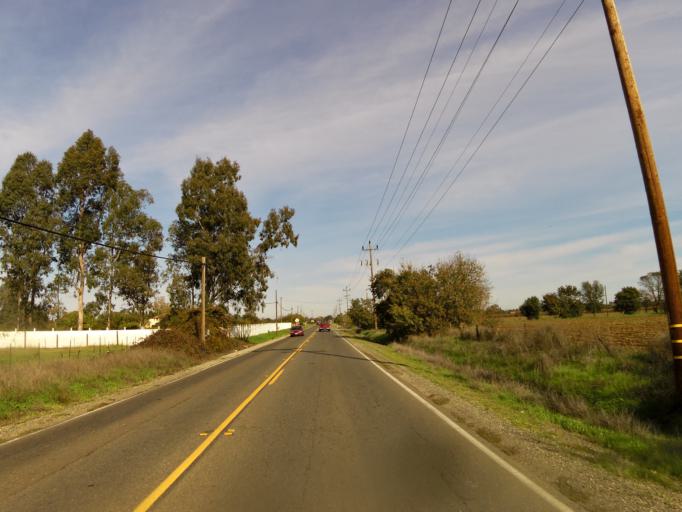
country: US
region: California
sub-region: Sacramento County
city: Wilton
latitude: 38.4133
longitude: -121.3203
